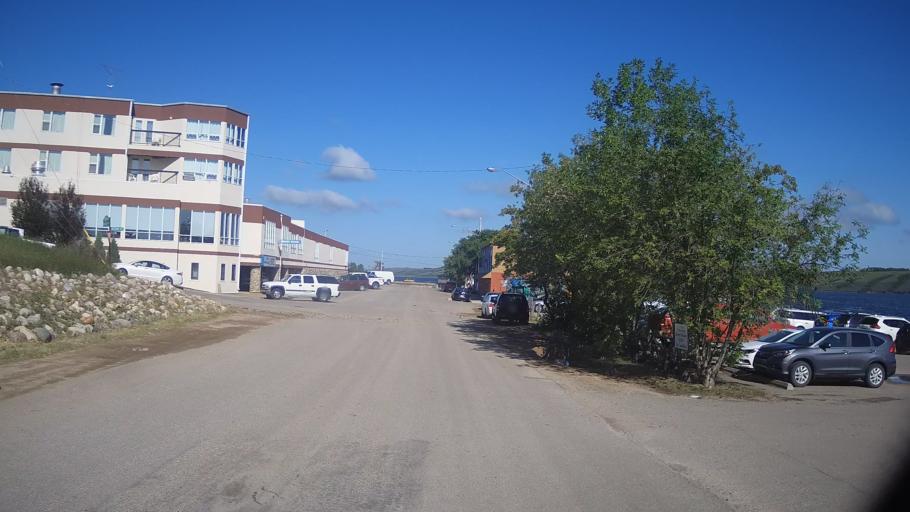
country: CA
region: Saskatchewan
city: Watrous
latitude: 51.7205
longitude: -105.4439
